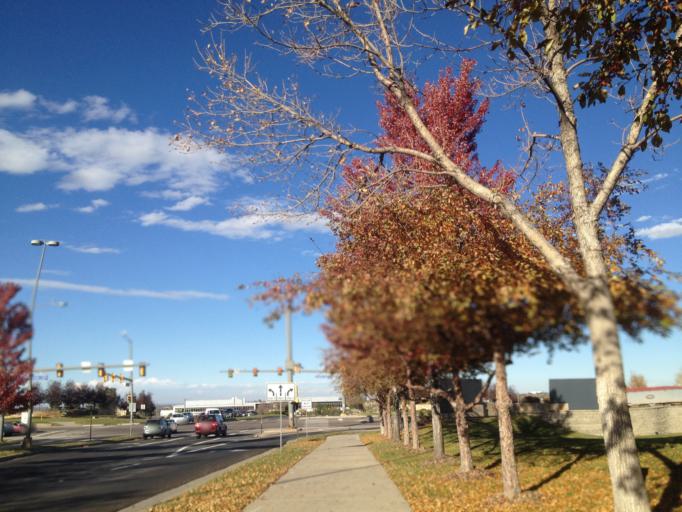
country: US
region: Colorado
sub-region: Broomfield County
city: Broomfield
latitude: 39.9152
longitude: -105.1059
